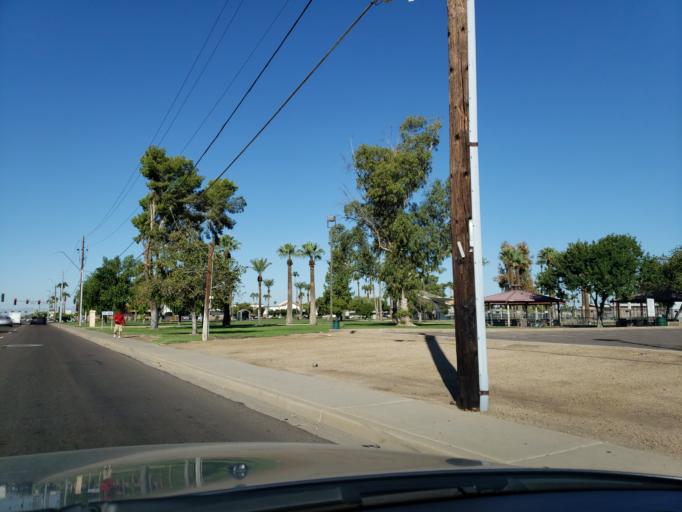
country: US
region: Arizona
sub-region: Maricopa County
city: Glendale
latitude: 33.5242
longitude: -112.1844
